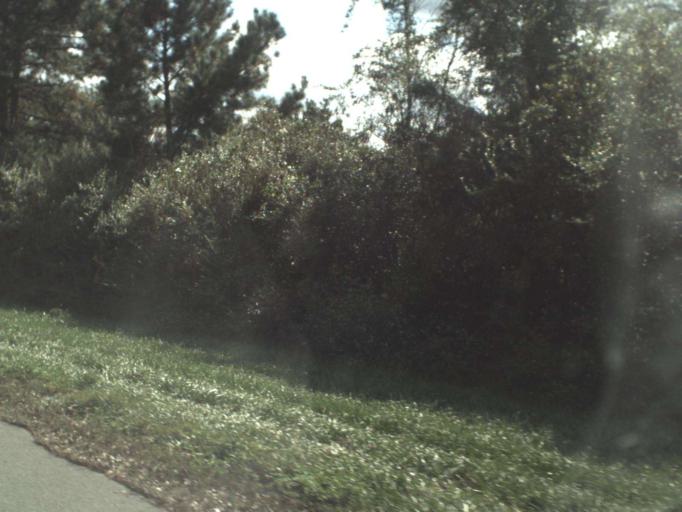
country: US
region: Florida
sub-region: Gadsden County
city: Gretna
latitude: 30.6458
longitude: -84.6790
